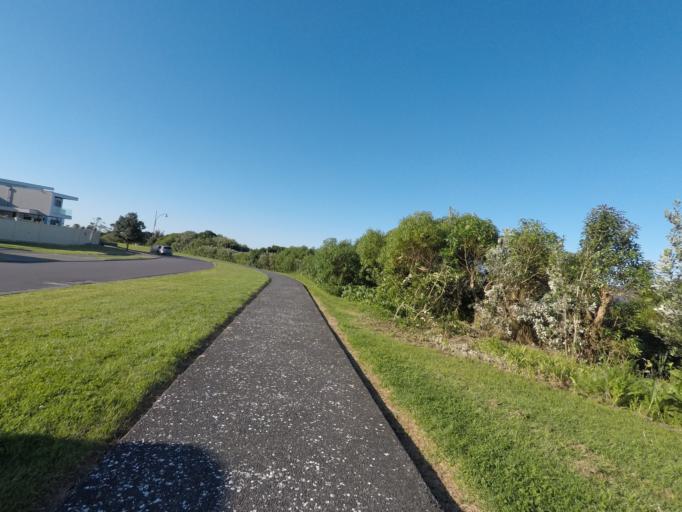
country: NZ
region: Auckland
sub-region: Auckland
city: Rosebank
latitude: -36.8350
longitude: 174.6619
